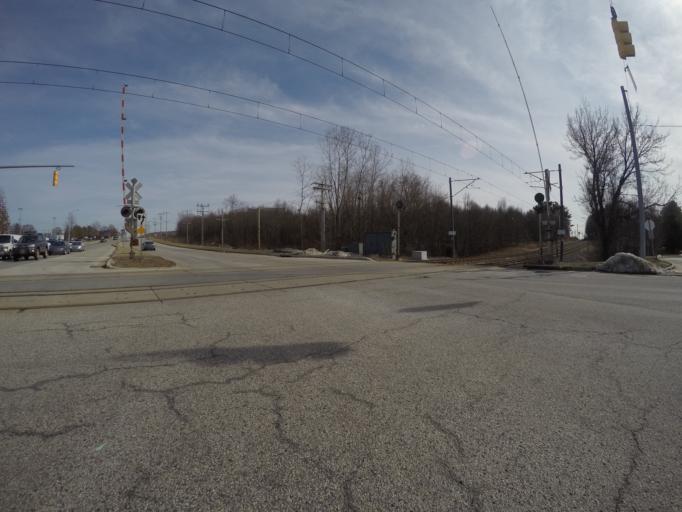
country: US
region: Maryland
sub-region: Baltimore County
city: Hunt Valley
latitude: 39.4956
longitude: -76.6528
